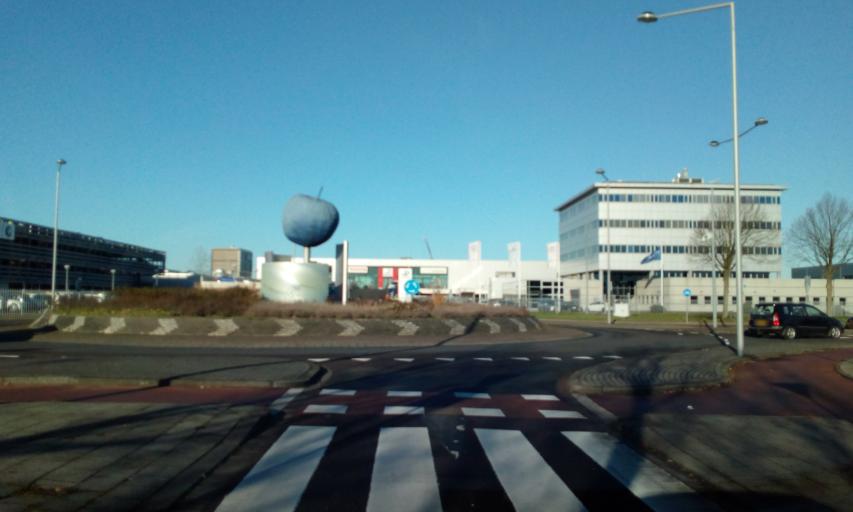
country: NL
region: South Holland
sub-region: Gemeente Leidschendam-Voorburg
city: Voorburg
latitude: 52.0685
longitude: 4.3906
